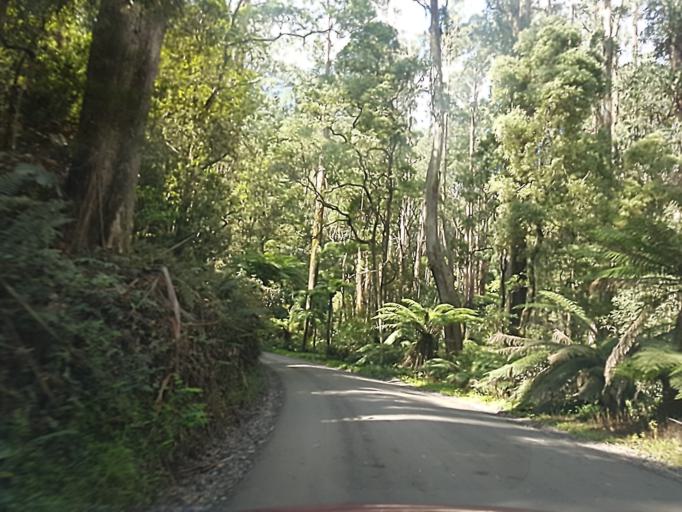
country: AU
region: Victoria
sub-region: Yarra Ranges
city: Kallista
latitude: -37.8781
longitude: 145.3757
